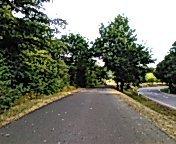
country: DE
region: Rheinland-Pfalz
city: Oberbillig
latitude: 49.7249
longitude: 6.5132
